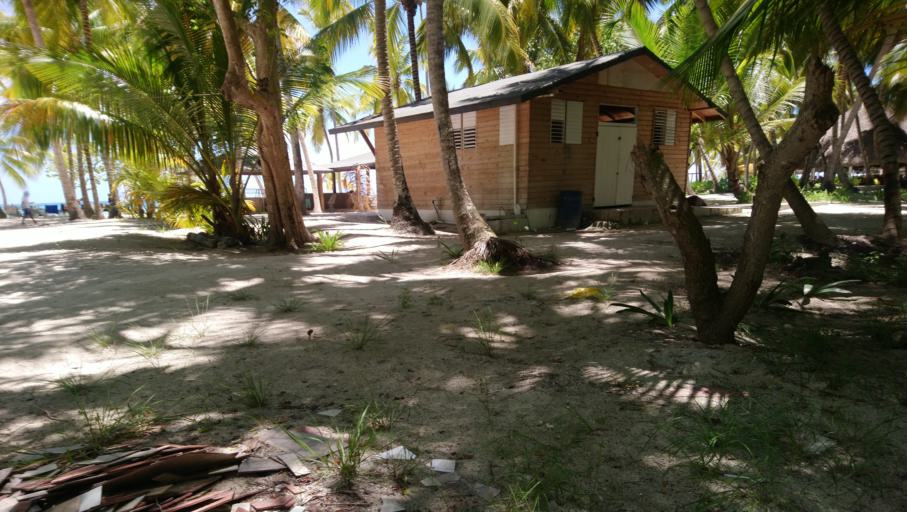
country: DO
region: La Altagracia
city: Boca de Yuma
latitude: 18.1717
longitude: -68.7803
